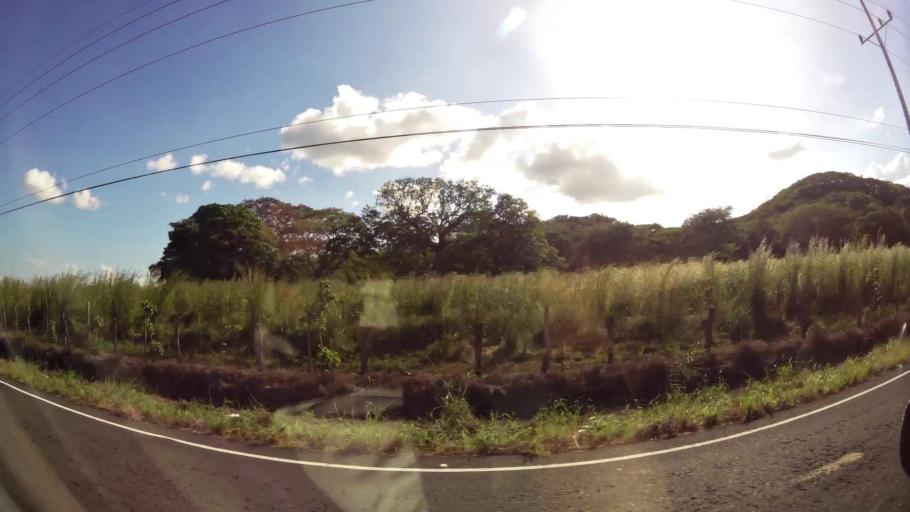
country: CR
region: Guanacaste
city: Sardinal
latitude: 10.5741
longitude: -85.6262
